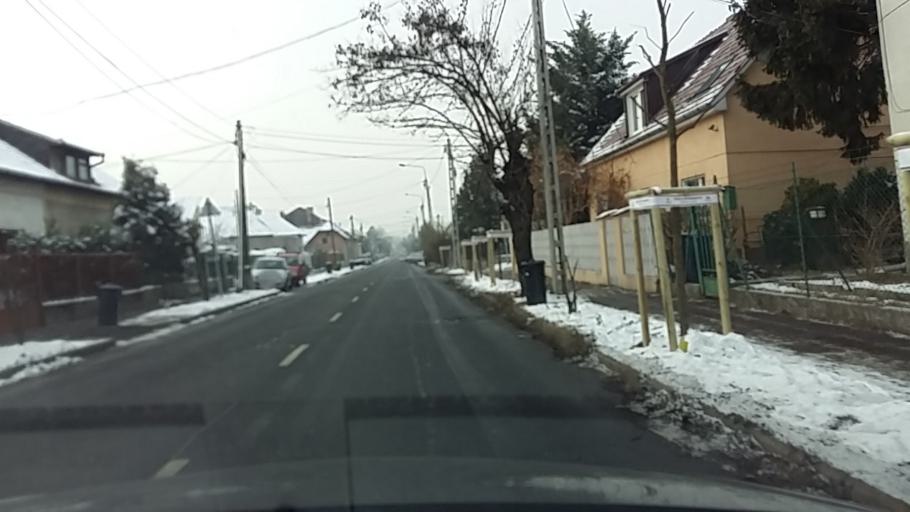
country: HU
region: Budapest
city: Budapest XIX. keruelet
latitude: 47.4355
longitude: 19.1318
